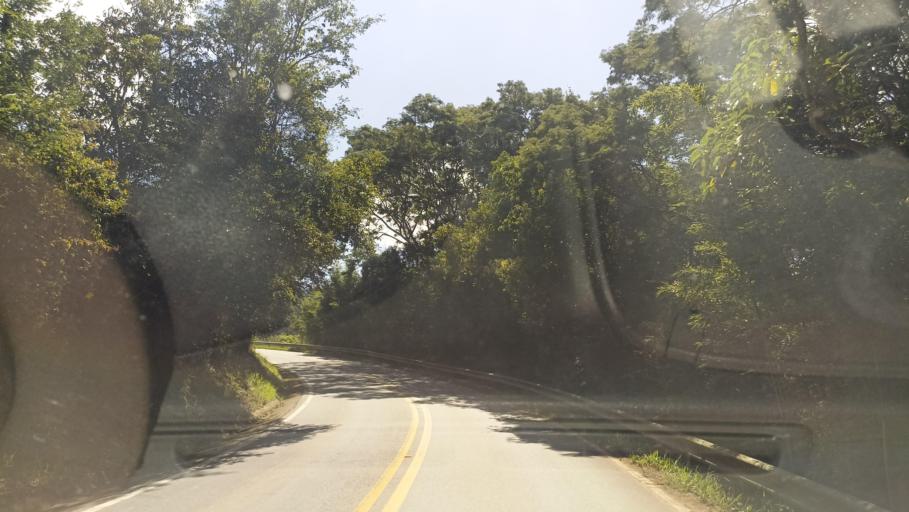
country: BR
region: Sao Paulo
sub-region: Cunha
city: Cunha
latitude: -23.1068
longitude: -44.9520
